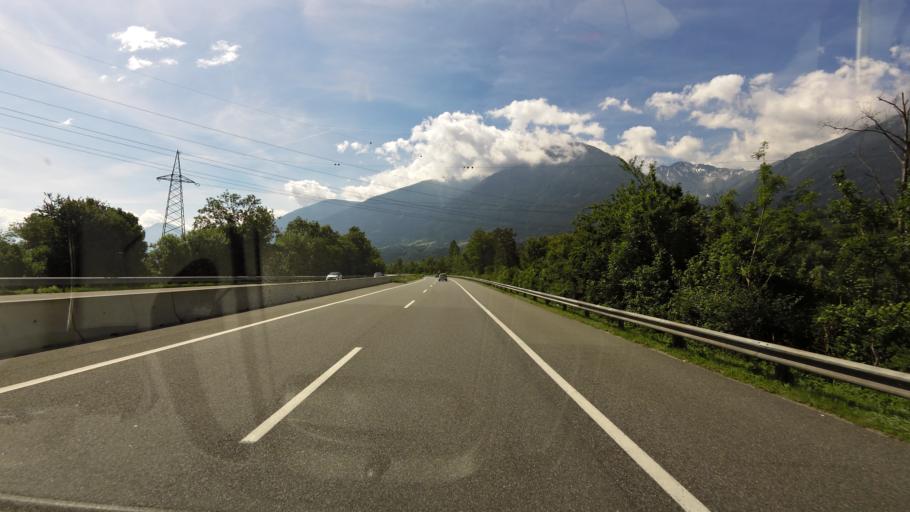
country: AT
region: Tyrol
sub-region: Politischer Bezirk Innsbruck Land
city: Pettnau
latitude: 47.3057
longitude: 11.1217
